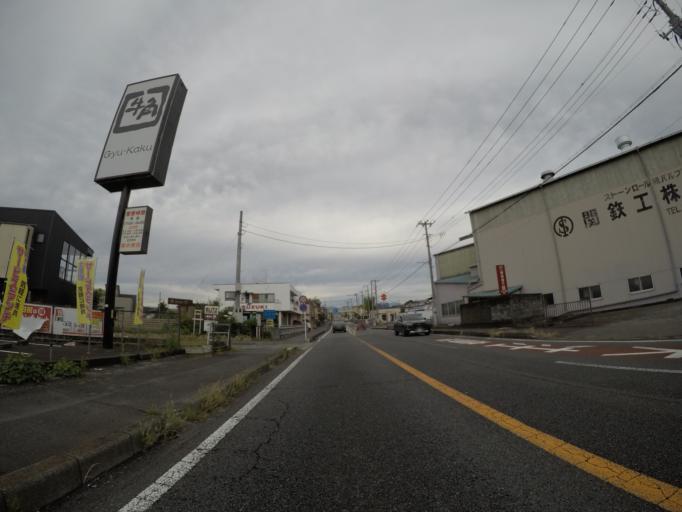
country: JP
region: Shizuoka
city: Fuji
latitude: 35.1887
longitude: 138.6524
